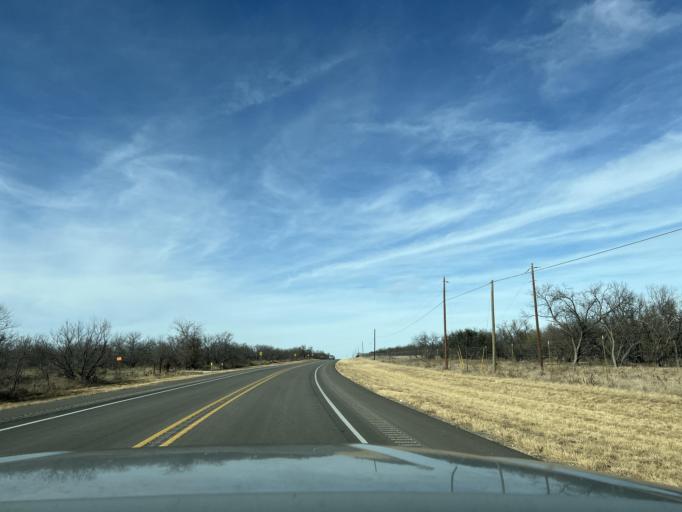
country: US
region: Texas
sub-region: Shackelford County
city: Albany
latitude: 32.6296
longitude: -99.2253
